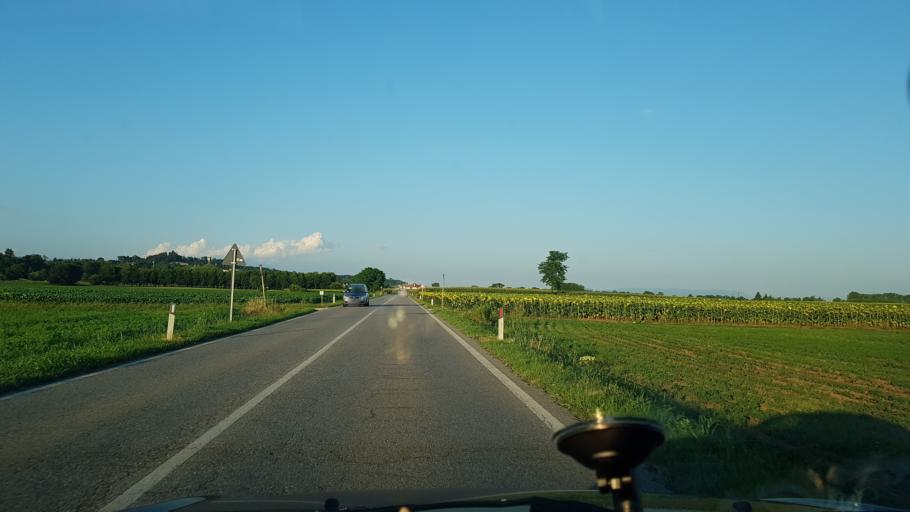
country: IT
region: Friuli Venezia Giulia
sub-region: Provincia di Udine
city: San Vito di Fagagna
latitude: 46.1084
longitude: 13.0656
